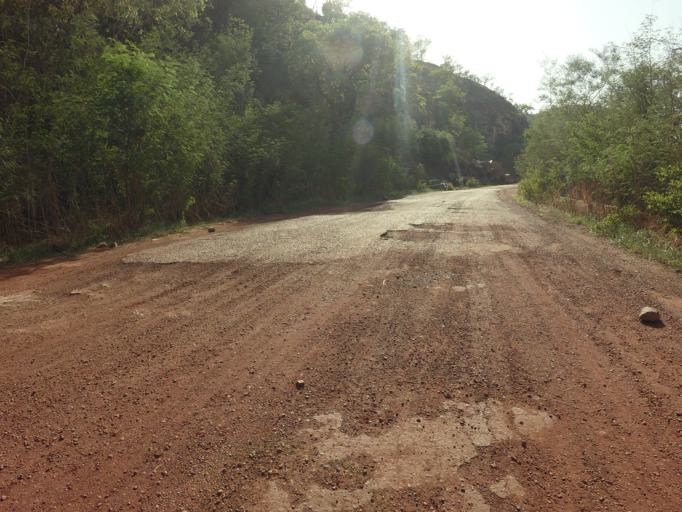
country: GH
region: Upper East
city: Bawku
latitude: 10.6414
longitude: -0.1946
